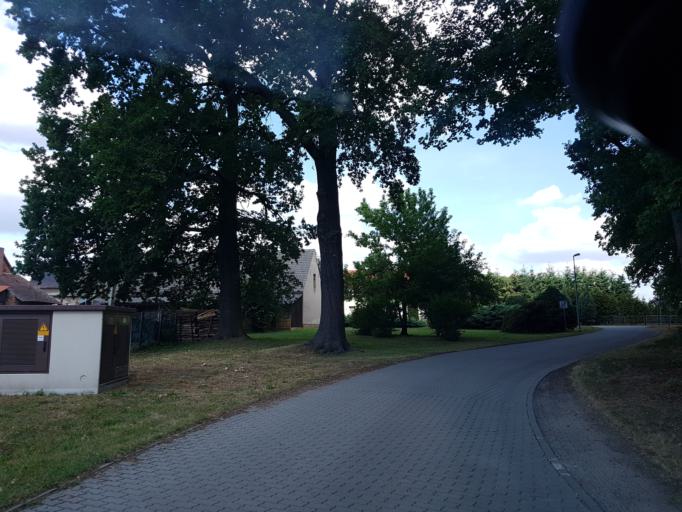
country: DE
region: Brandenburg
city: Altdobern
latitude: 51.6831
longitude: 14.0814
